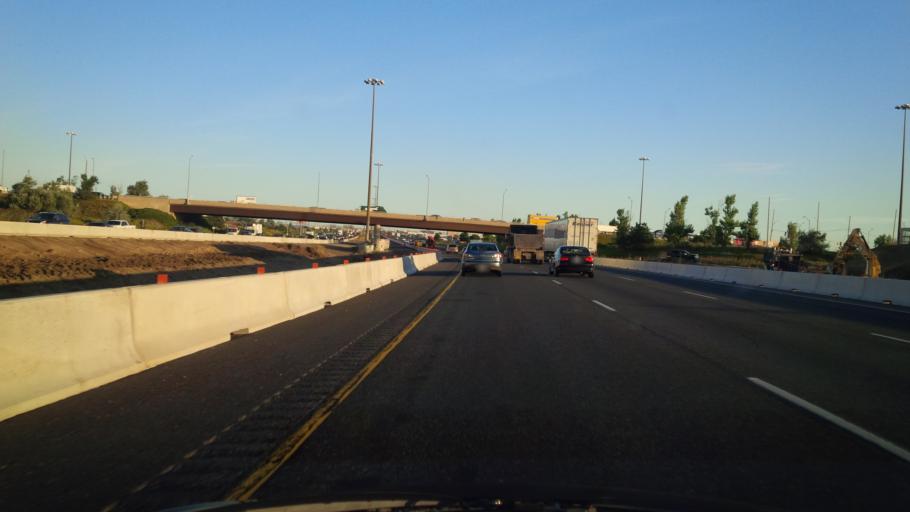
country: CA
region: Ontario
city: Brampton
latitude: 43.6842
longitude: -79.7097
